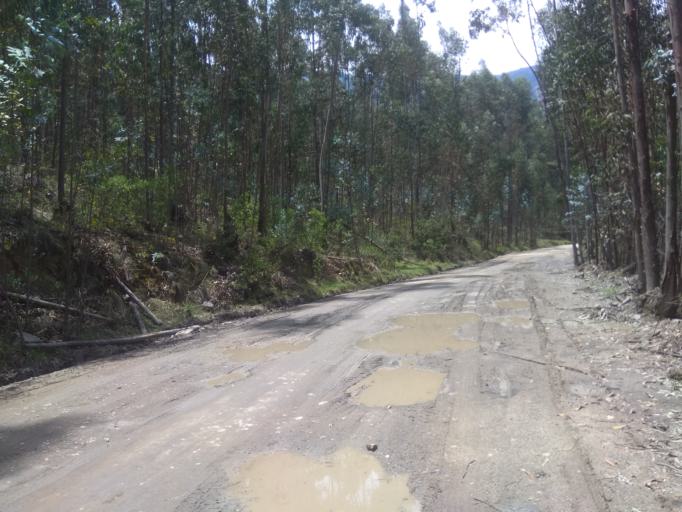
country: CO
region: Boyaca
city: Socha Viejo
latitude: 5.9743
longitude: -72.7373
